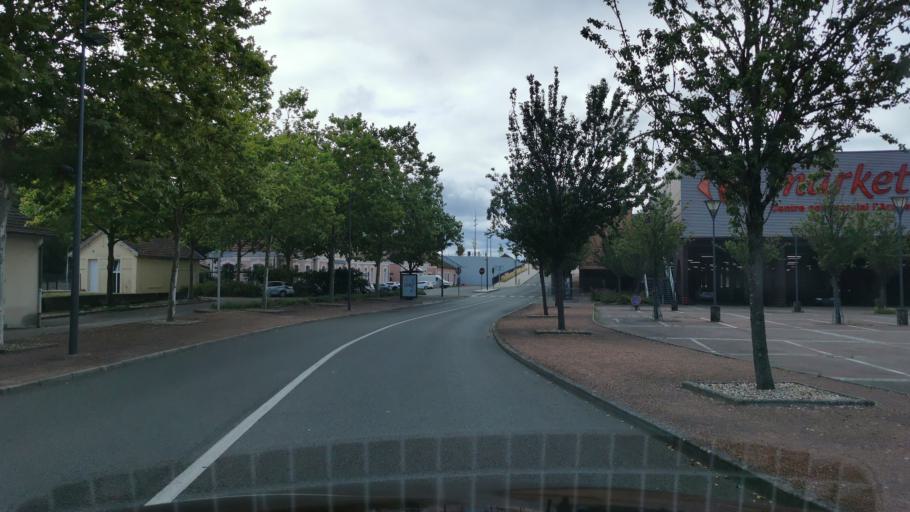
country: FR
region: Bourgogne
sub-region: Departement de Saone-et-Loire
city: Le Creusot
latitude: 46.8083
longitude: 4.4294
